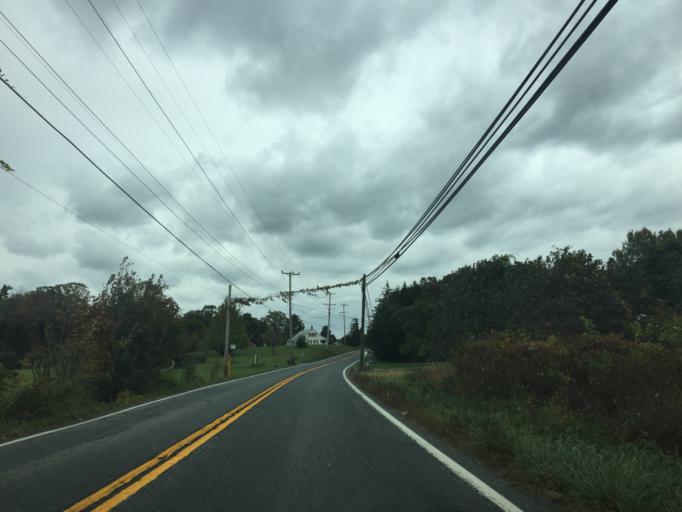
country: US
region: Maryland
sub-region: Harford County
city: Riverside
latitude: 39.5413
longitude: -76.2574
